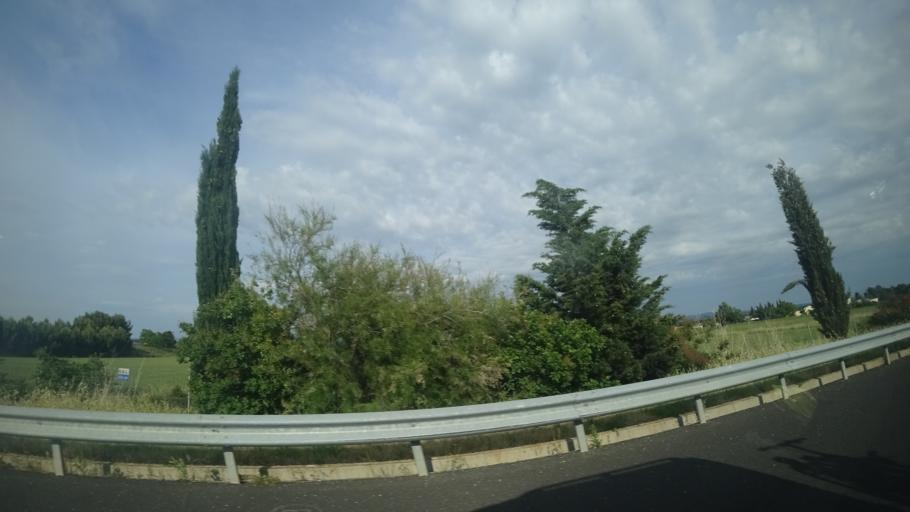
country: FR
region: Languedoc-Roussillon
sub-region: Departement de l'Herault
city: Nebian
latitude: 43.6337
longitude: 3.4478
